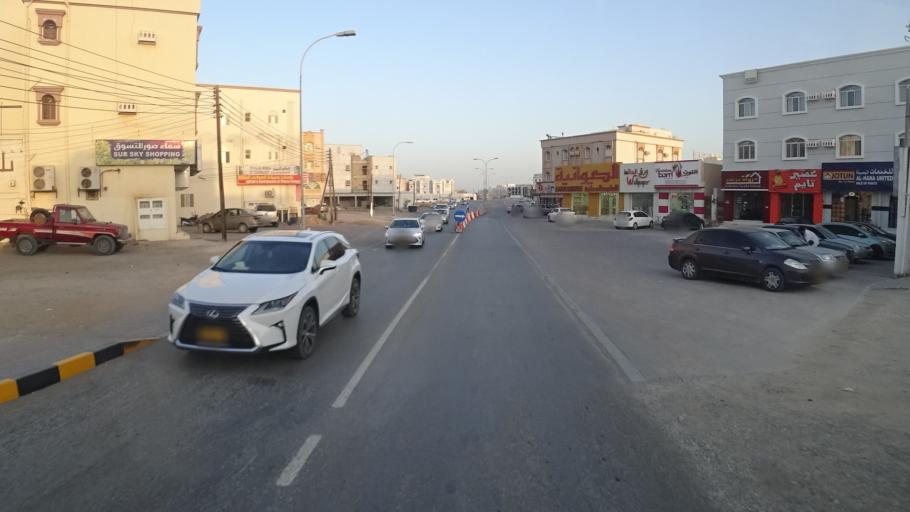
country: OM
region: Ash Sharqiyah
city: Sur
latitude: 22.5799
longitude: 59.5116
